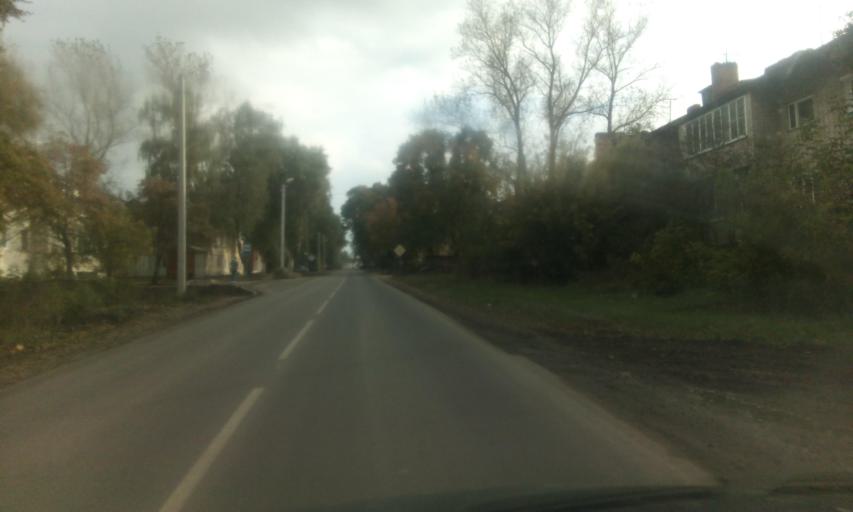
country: RU
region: Tula
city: Partizan
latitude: 53.9535
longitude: 38.0970
